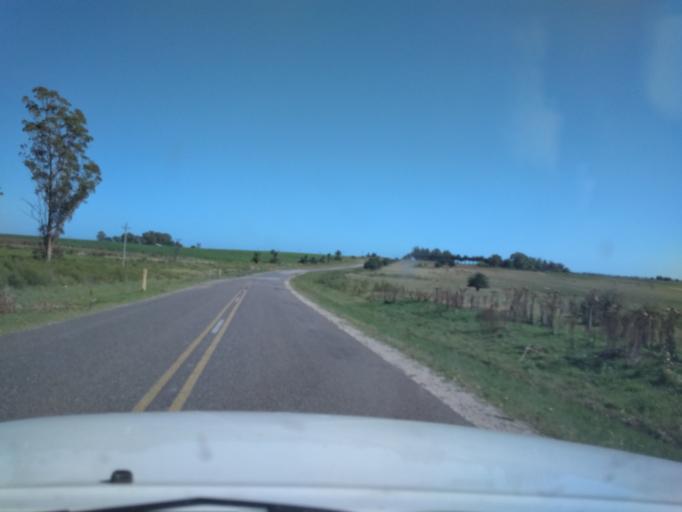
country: UY
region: Canelones
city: San Ramon
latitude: -34.1638
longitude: -55.9468
